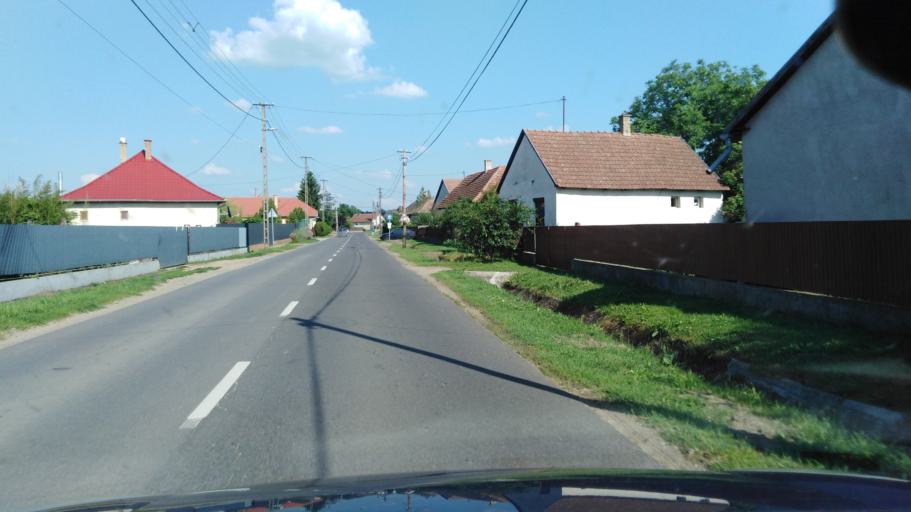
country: HU
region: Szabolcs-Szatmar-Bereg
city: Nyirvasvari
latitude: 47.8265
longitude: 22.1794
